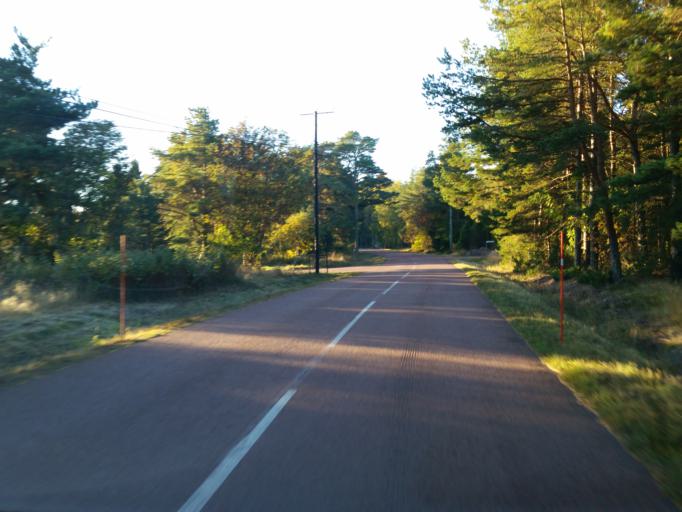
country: AX
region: Alands skaergard
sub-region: Vardoe
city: Vardoe
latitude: 60.2793
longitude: 20.3896
